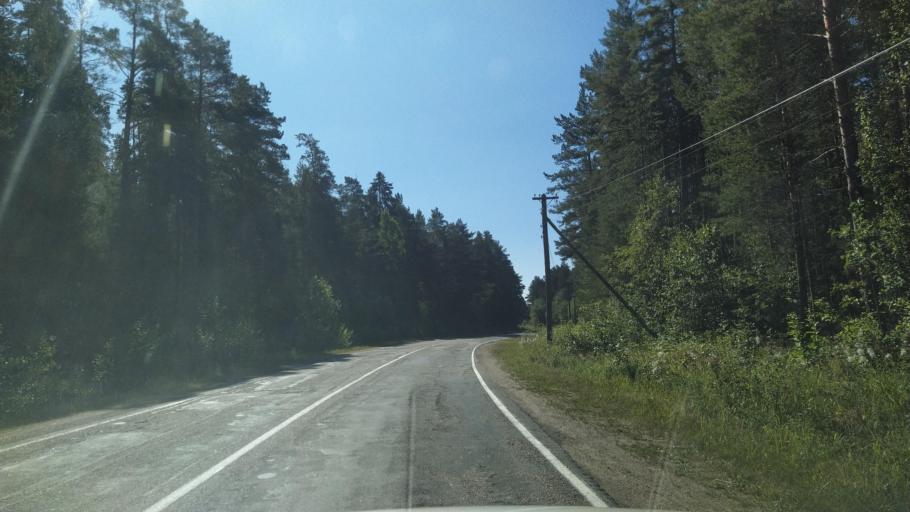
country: RU
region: Leningrad
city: Priozersk
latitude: 60.9705
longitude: 30.2840
